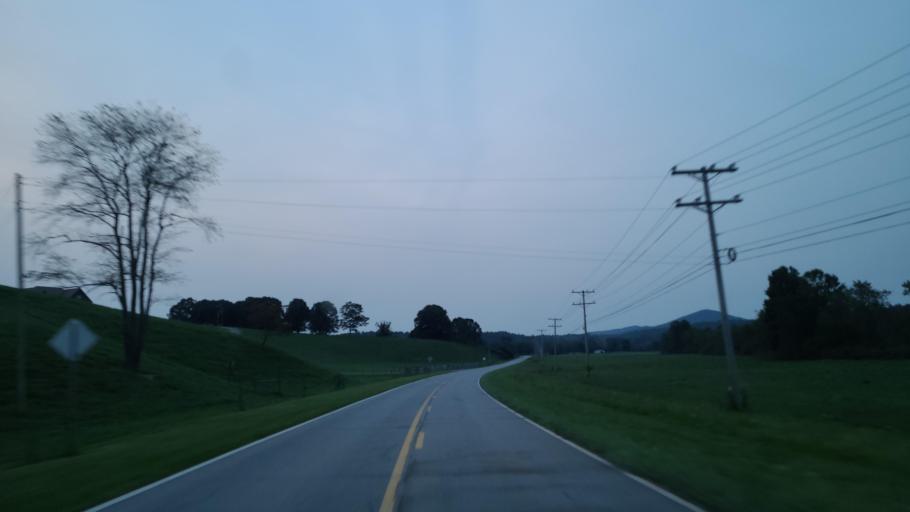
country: US
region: Georgia
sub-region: Union County
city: Blairsville
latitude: 34.8372
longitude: -84.0861
